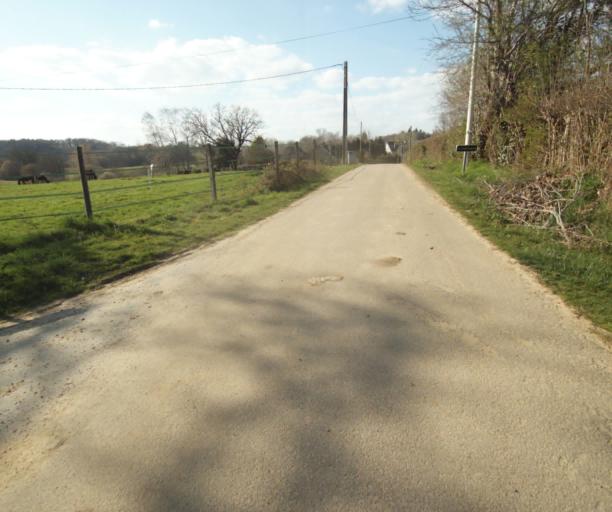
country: FR
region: Limousin
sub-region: Departement de la Correze
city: Saint-Mexant
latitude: 45.3259
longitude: 1.6134
